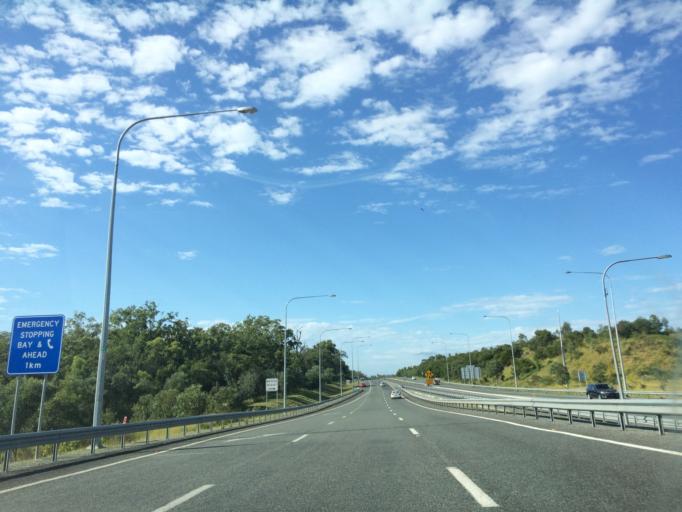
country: AU
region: Queensland
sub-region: Brisbane
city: Forest Lake
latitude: -27.6286
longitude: 152.9411
